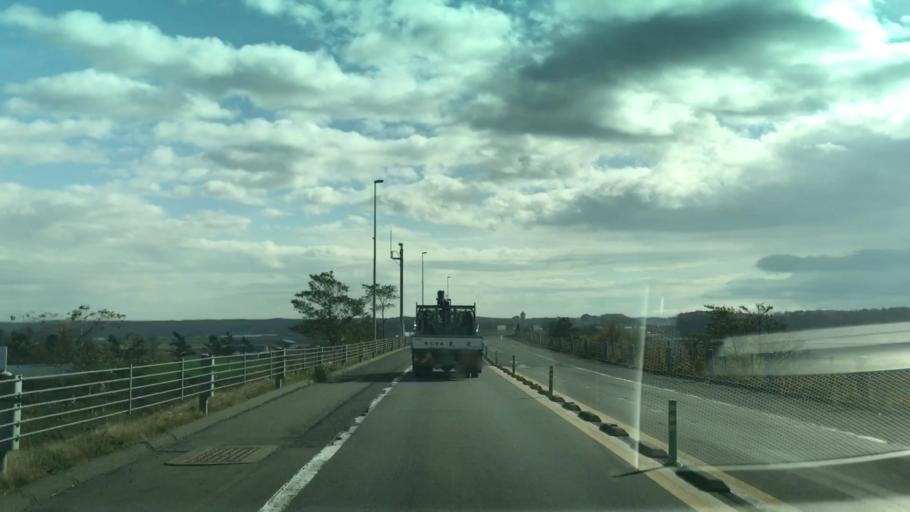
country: JP
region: Hokkaido
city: Tomakomai
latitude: 42.5751
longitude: 141.9690
